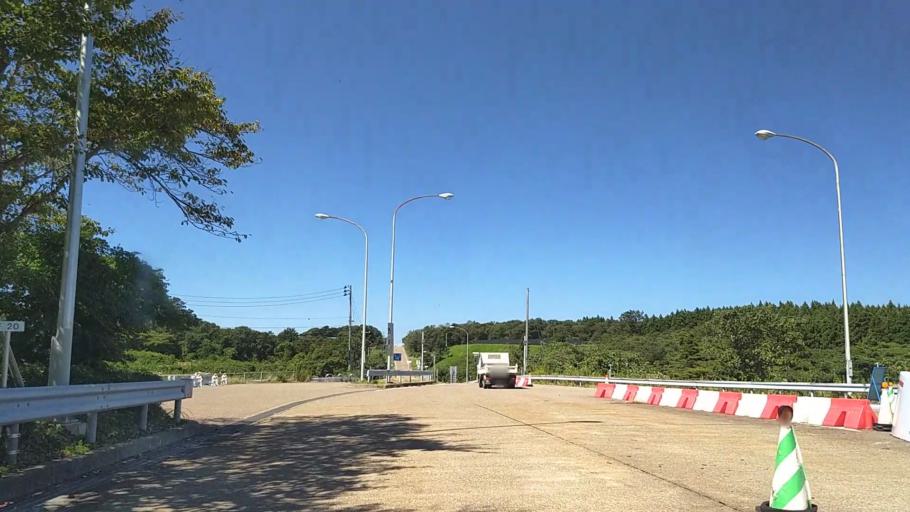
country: JP
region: Niigata
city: Joetsu
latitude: 37.1685
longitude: 138.1115
